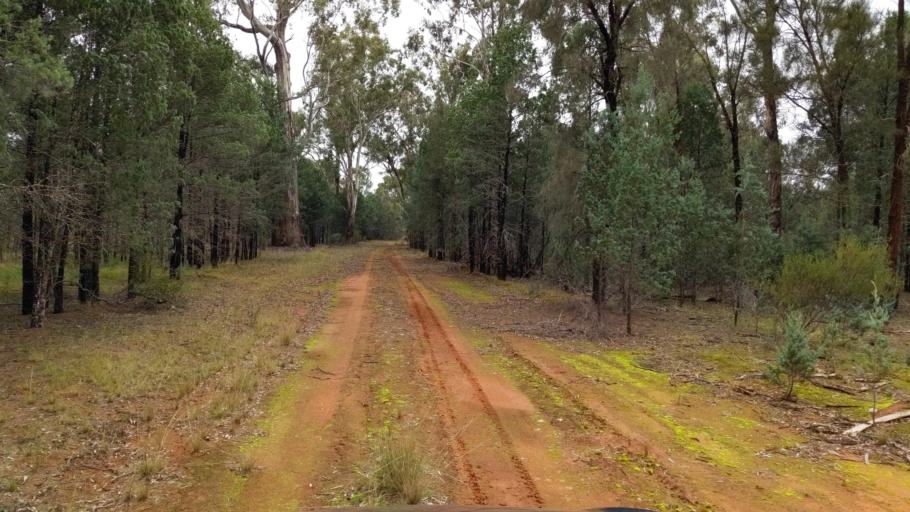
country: AU
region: New South Wales
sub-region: Coolamon
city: Coolamon
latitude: -34.8427
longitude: 146.9333
